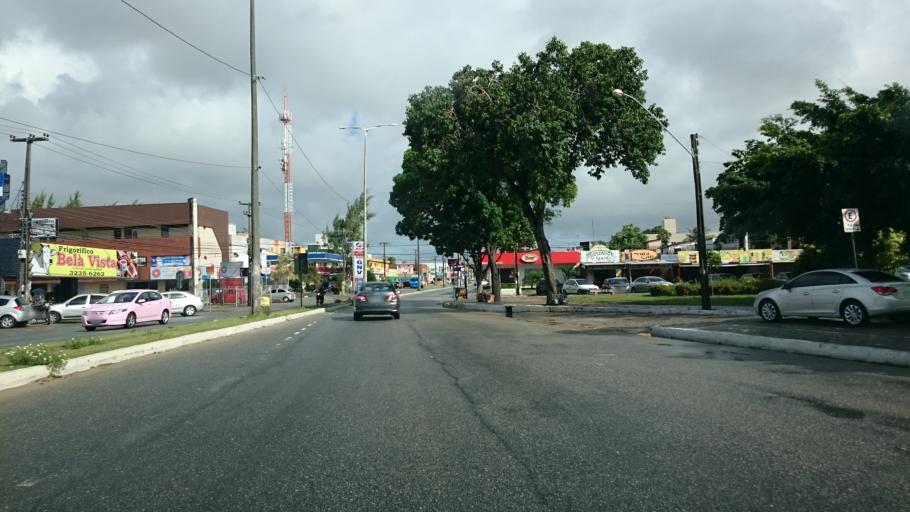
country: BR
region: Paraiba
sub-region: Joao Pessoa
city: Joao Pessoa
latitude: -7.1480
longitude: -34.8438
